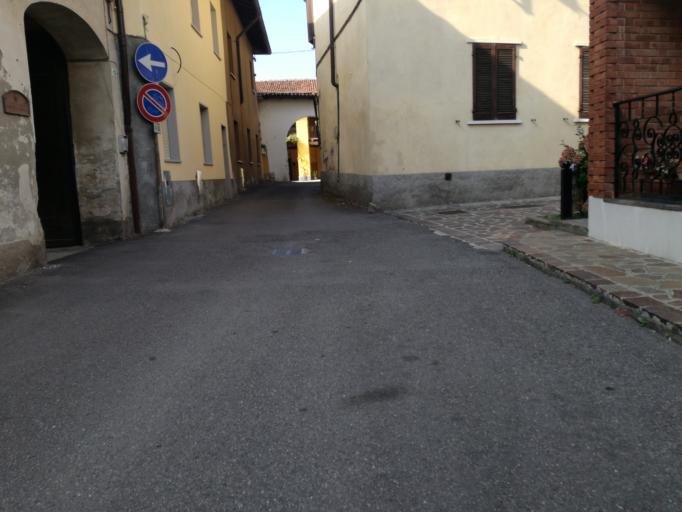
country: IT
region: Lombardy
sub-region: Provincia di Lecco
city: Paderno d'Adda
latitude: 45.6807
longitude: 9.4438
